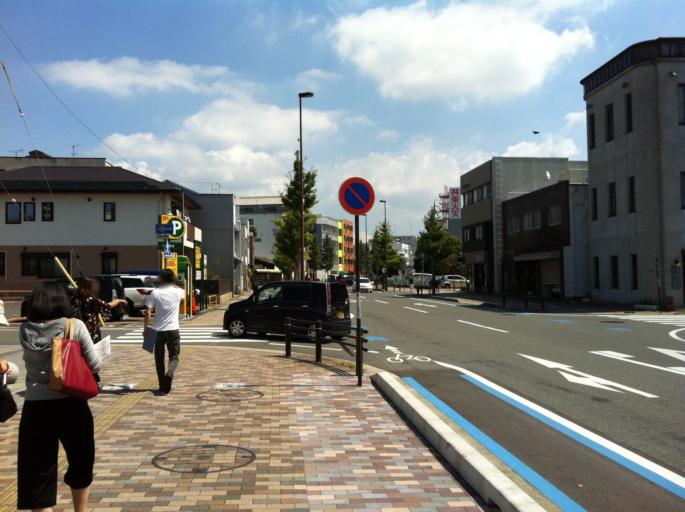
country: JP
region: Aichi
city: Toyohashi
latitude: 34.7681
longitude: 137.3845
